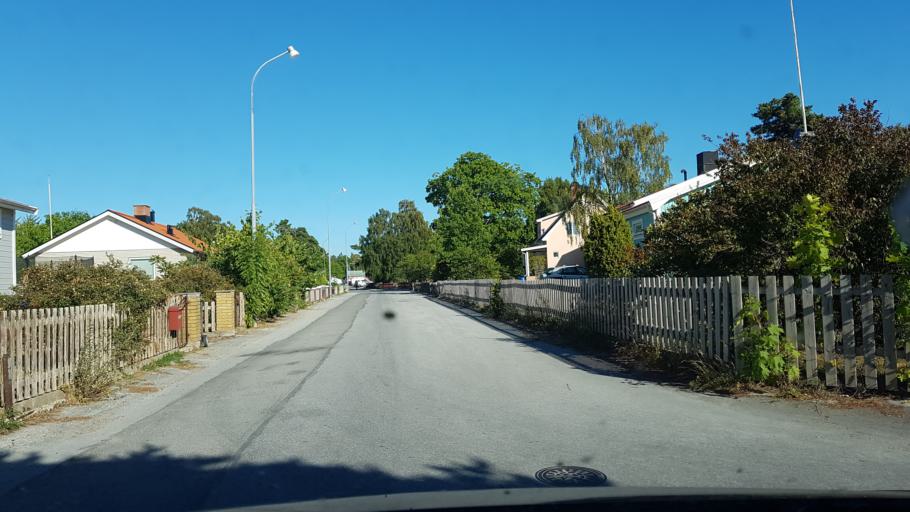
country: SE
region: Gotland
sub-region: Gotland
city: Vibble
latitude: 57.6021
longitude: 18.2469
